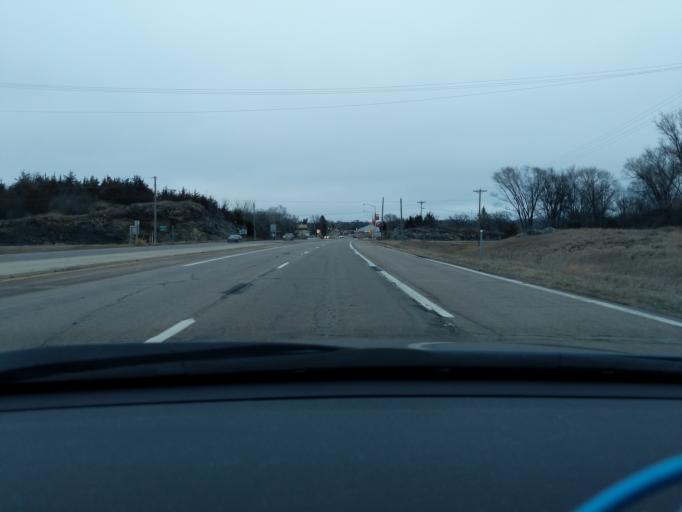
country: US
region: Minnesota
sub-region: Yellow Medicine County
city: Granite Falls
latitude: 44.8018
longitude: -95.5474
